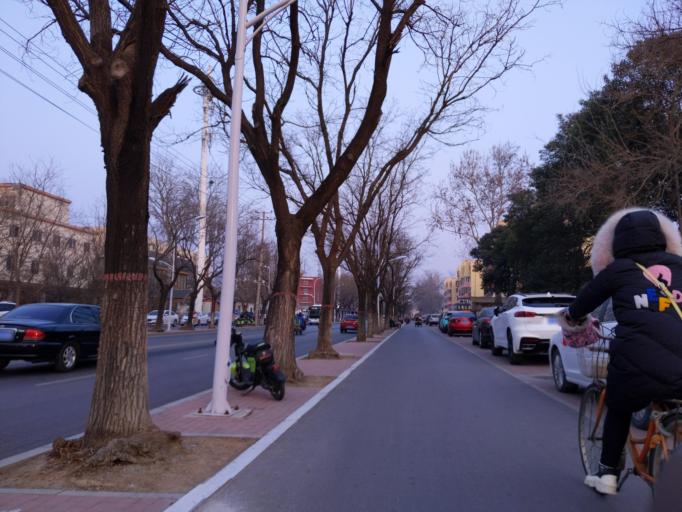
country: CN
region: Henan Sheng
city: Zhongyuanlu
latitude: 35.7695
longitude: 115.0931
